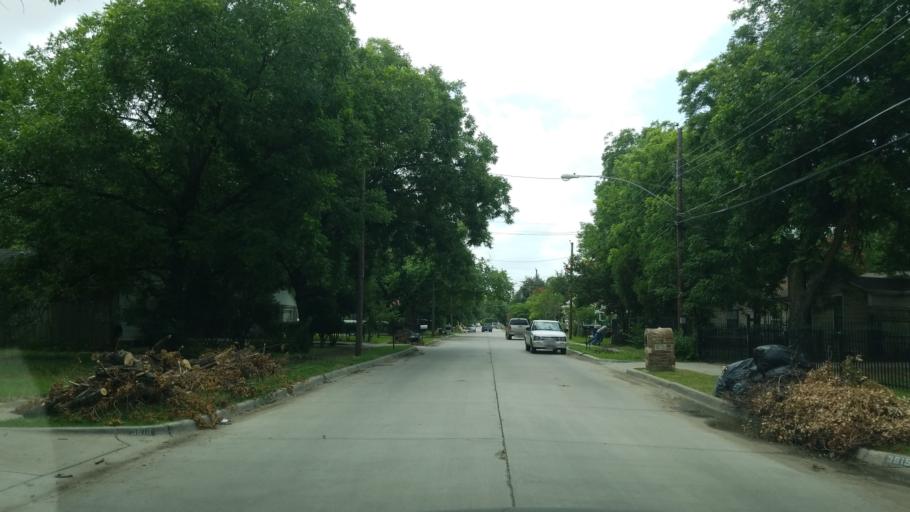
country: US
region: Texas
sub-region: Dallas County
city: Cockrell Hill
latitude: 32.7868
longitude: -96.9024
